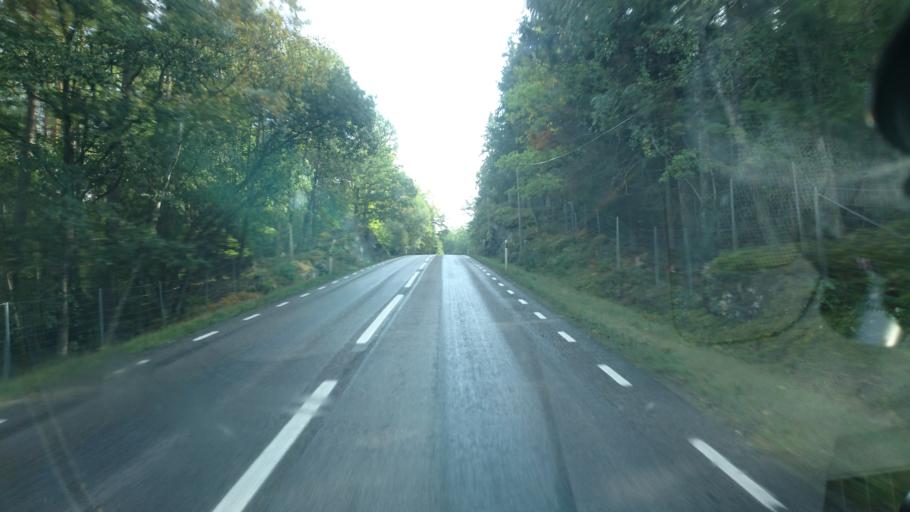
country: SE
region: Vaestra Goetaland
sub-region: Alingsas Kommun
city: Sollebrunn
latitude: 58.1365
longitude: 12.4540
